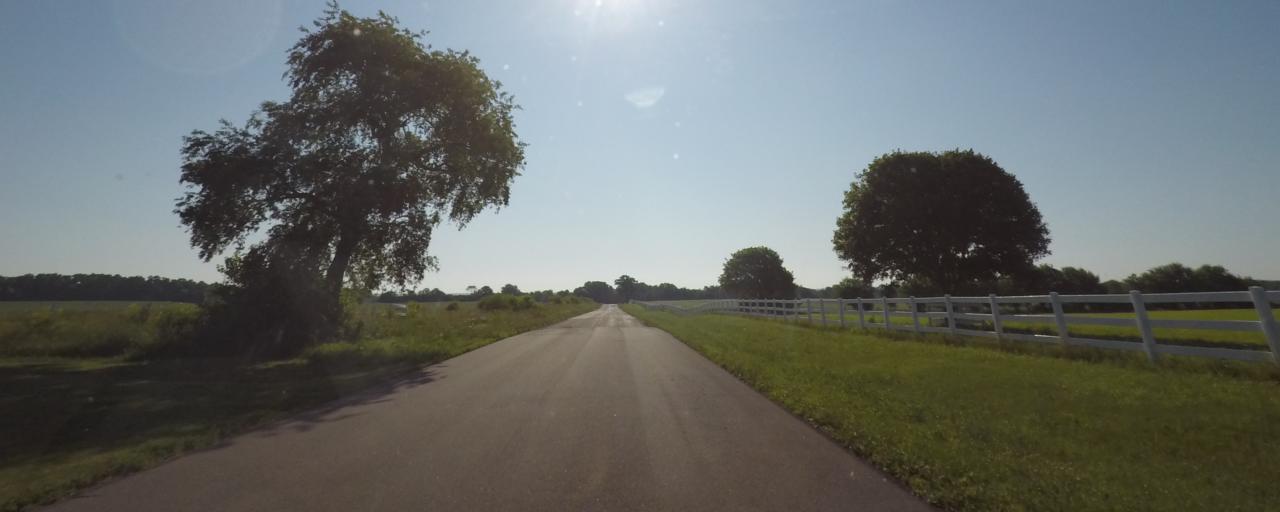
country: US
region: Wisconsin
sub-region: Jefferson County
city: Palmyra
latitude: 42.9190
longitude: -88.5540
